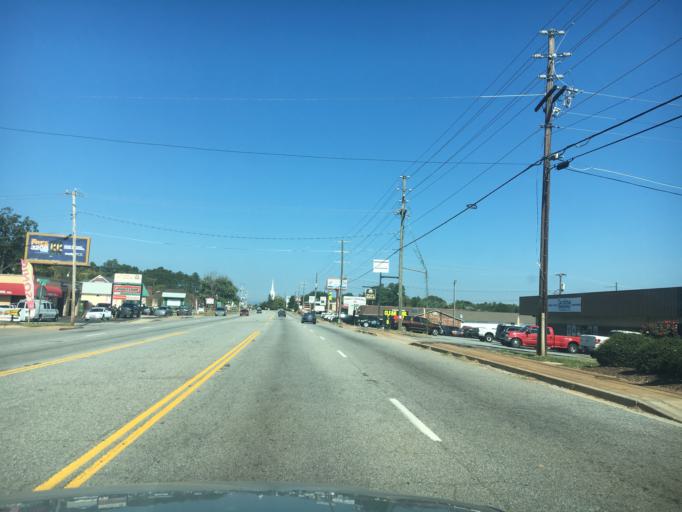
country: US
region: South Carolina
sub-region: Spartanburg County
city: Boiling Springs
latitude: 35.0398
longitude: -81.9751
